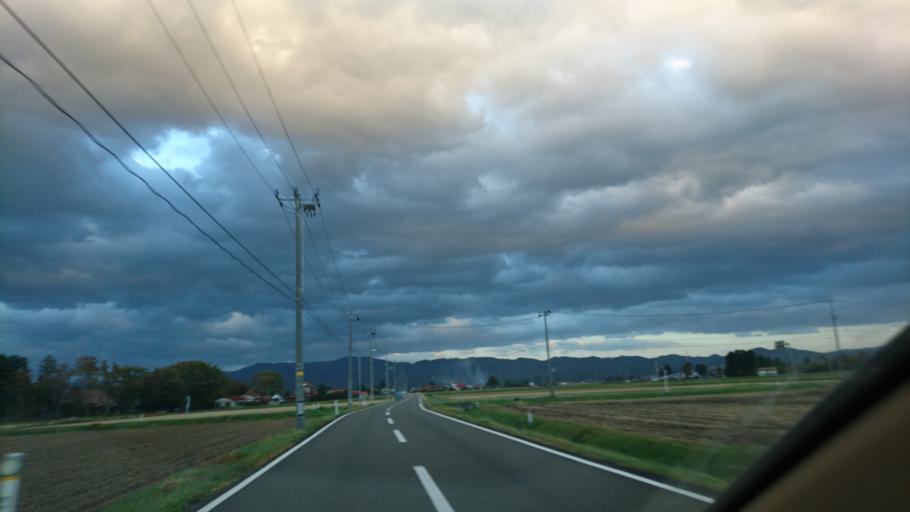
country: JP
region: Iwate
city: Mizusawa
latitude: 39.0908
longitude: 141.1456
